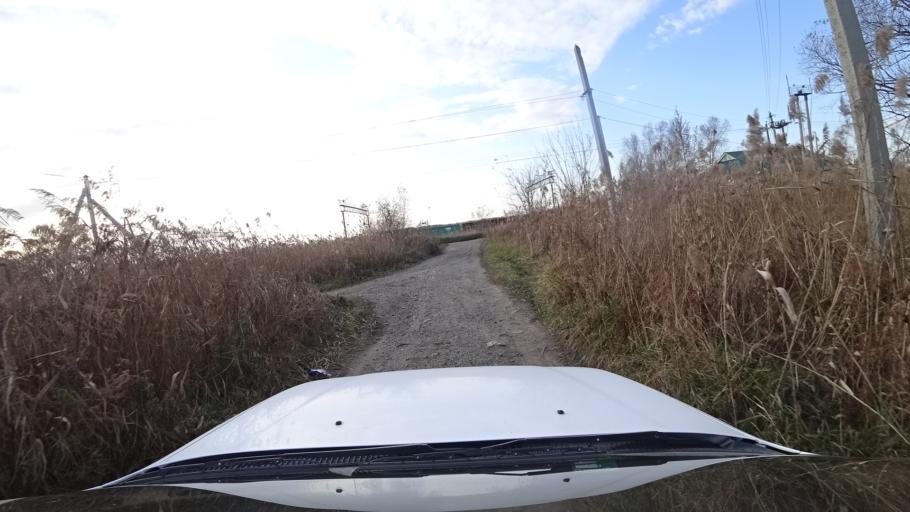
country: RU
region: Primorskiy
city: Lazo
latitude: 45.8208
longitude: 133.6124
